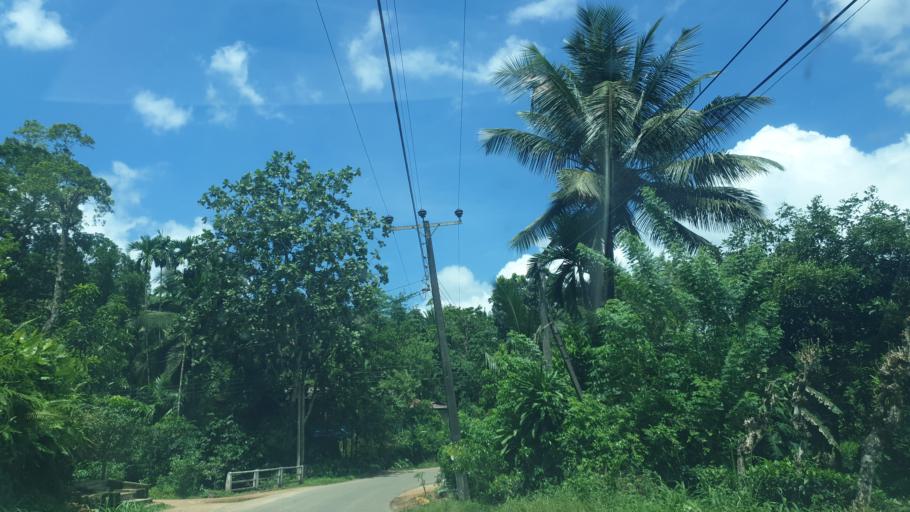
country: LK
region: Sabaragamuwa
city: Ratnapura
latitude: 6.4684
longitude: 80.4266
